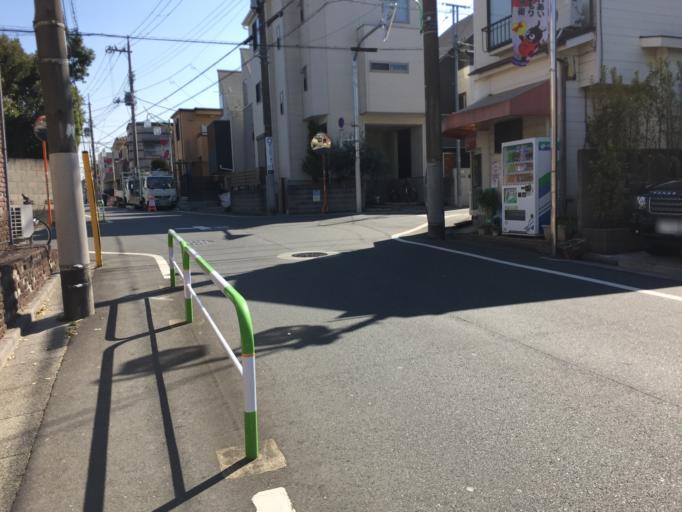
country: JP
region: Tokyo
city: Tokyo
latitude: 35.6192
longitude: 139.6512
